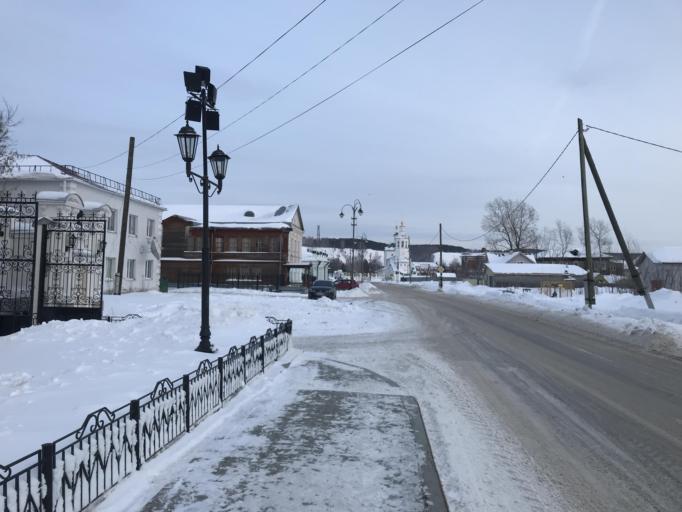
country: RU
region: Tjumen
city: Tobol'sk
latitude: 58.1931
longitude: 68.2442
